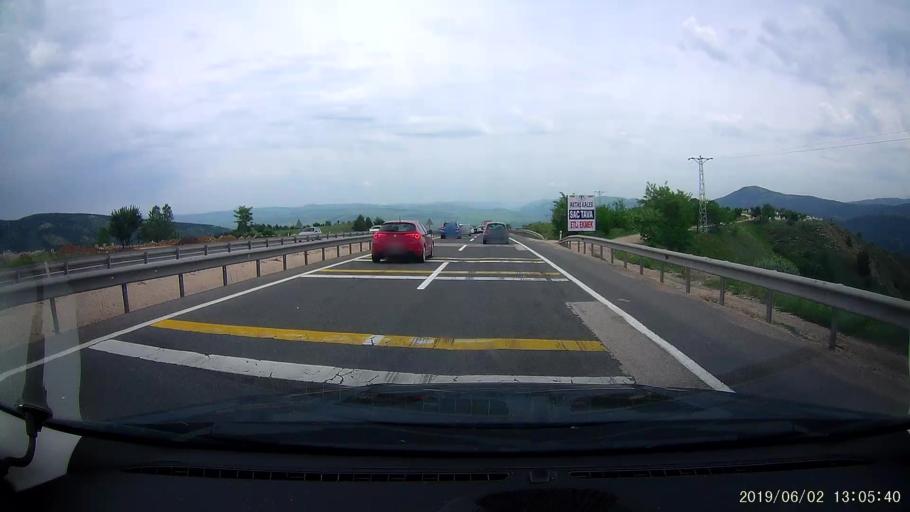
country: TR
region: Karabuk
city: Gozyeri
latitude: 40.8598
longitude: 32.5421
